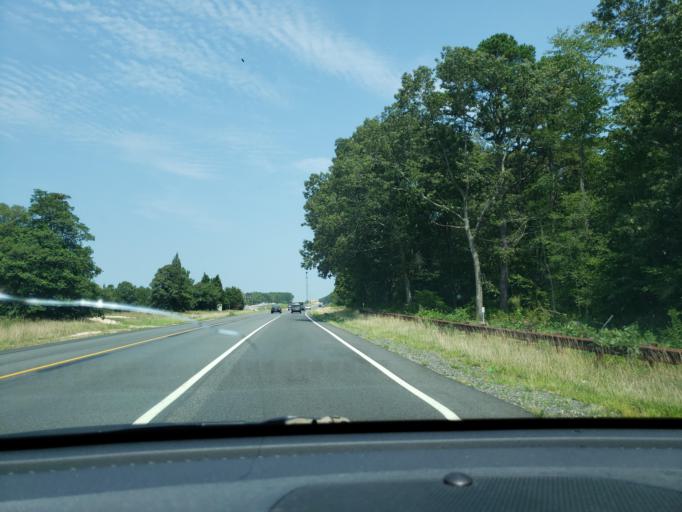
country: US
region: New Jersey
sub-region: Atlantic County
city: Somers Point
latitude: 39.3385
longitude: -74.6056
